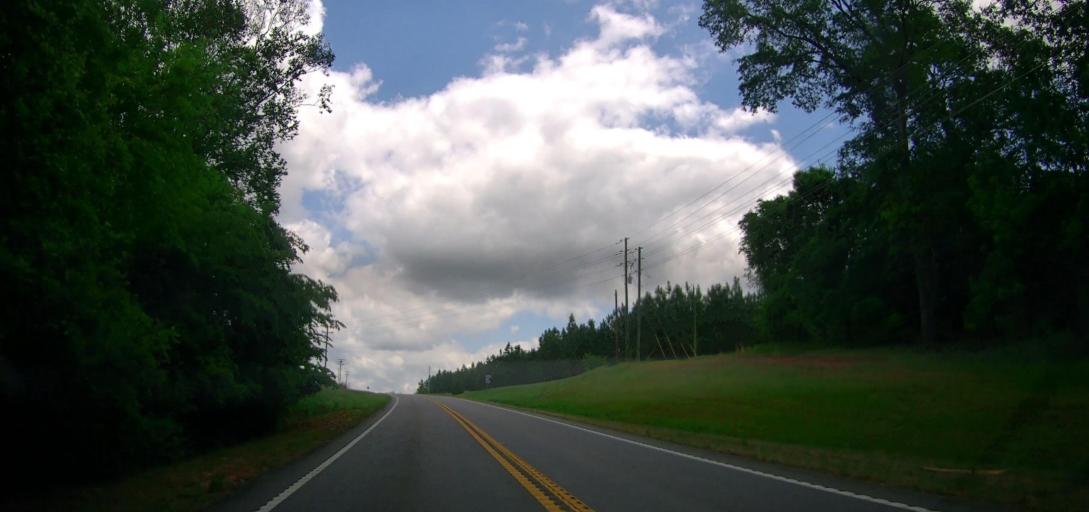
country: US
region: Georgia
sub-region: Laurens County
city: Dublin
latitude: 32.5534
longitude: -83.0511
